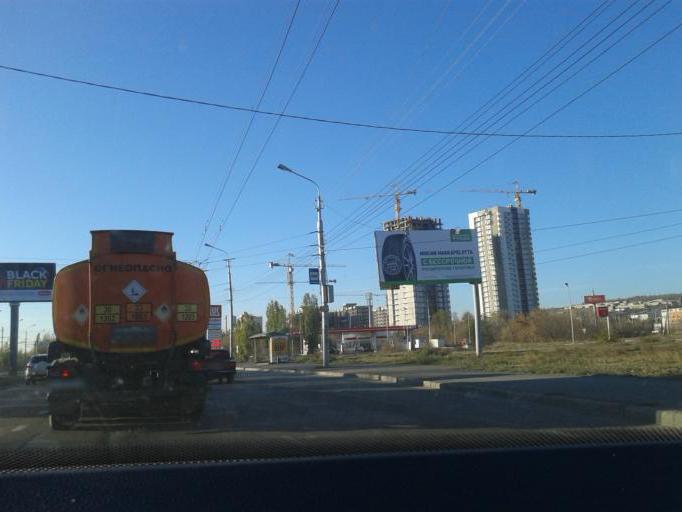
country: RU
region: Volgograd
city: Volgograd
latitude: 48.6286
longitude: 44.4273
